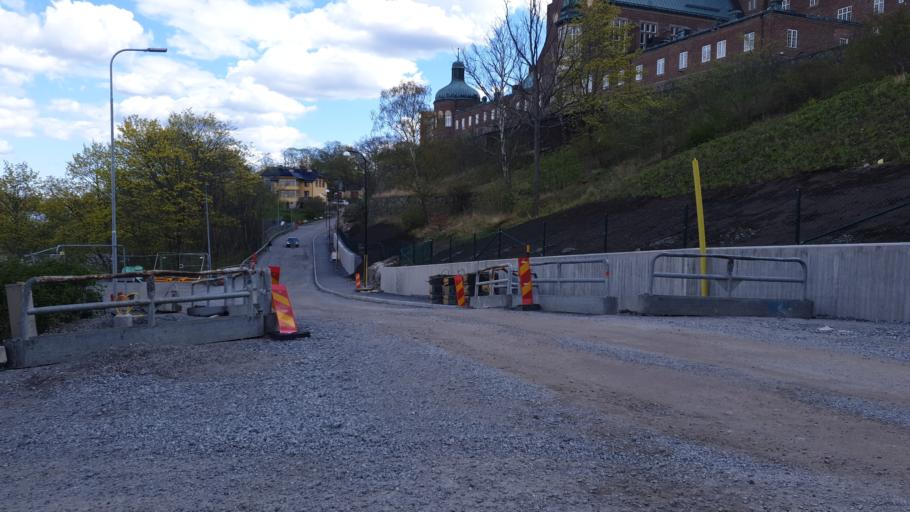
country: SE
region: Stockholm
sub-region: Stockholms Kommun
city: OEstermalm
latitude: 59.3156
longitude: 18.1161
